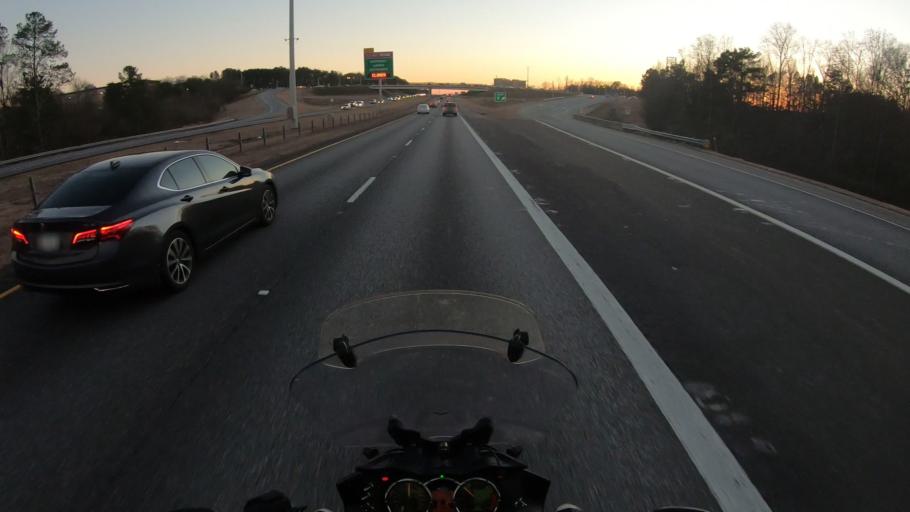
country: US
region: Georgia
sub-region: Cherokee County
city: Holly Springs
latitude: 34.1496
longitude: -84.5152
